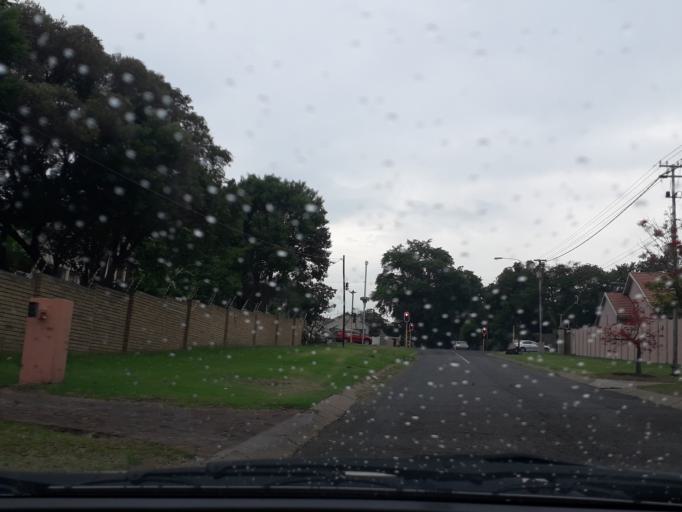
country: ZA
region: Gauteng
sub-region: City of Johannesburg Metropolitan Municipality
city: Modderfontein
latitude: -26.1358
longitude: 28.1041
